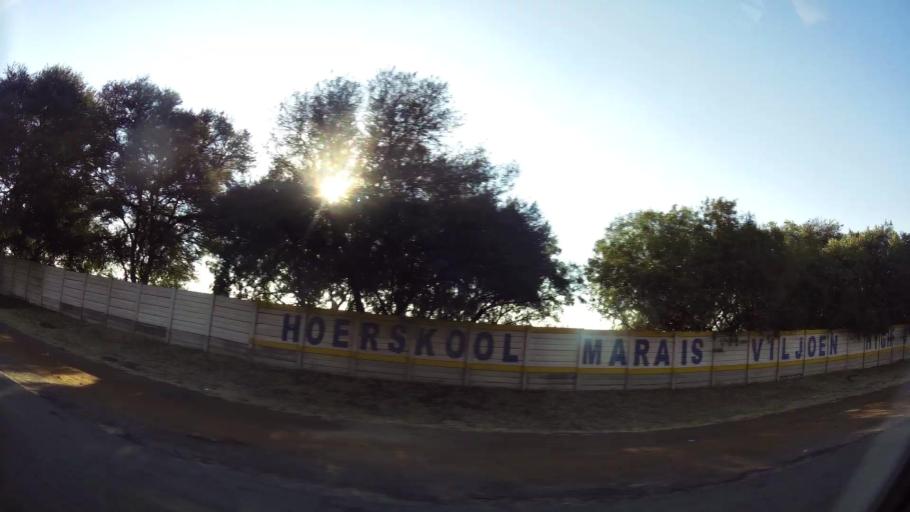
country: ZA
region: Gauteng
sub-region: Ekurhuleni Metropolitan Municipality
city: Germiston
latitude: -26.2723
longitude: 28.1033
